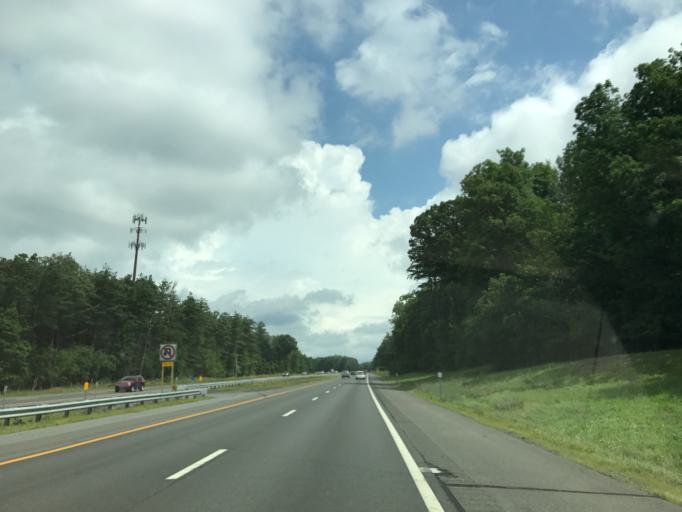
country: US
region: New York
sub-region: Greene County
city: Coxsackie
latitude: 42.3262
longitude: -73.8632
